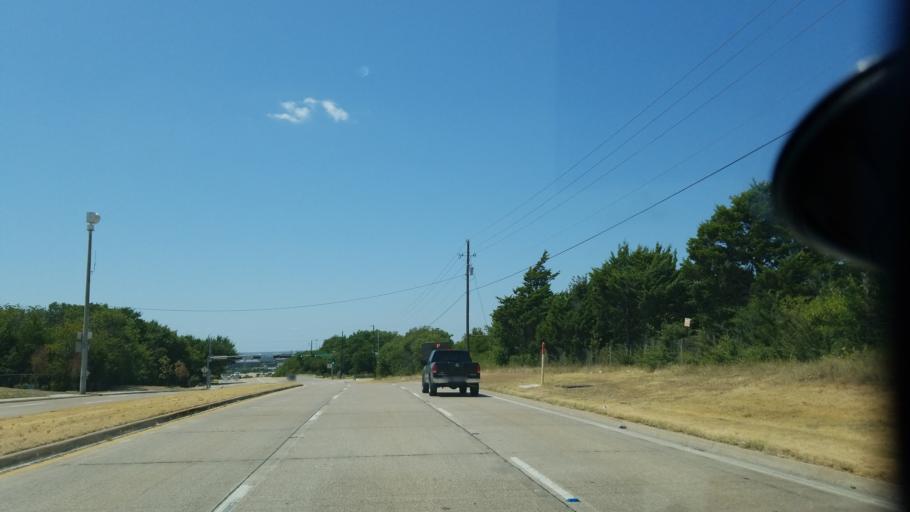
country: US
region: Texas
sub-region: Dallas County
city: Cockrell Hill
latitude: 32.7060
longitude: -96.9239
